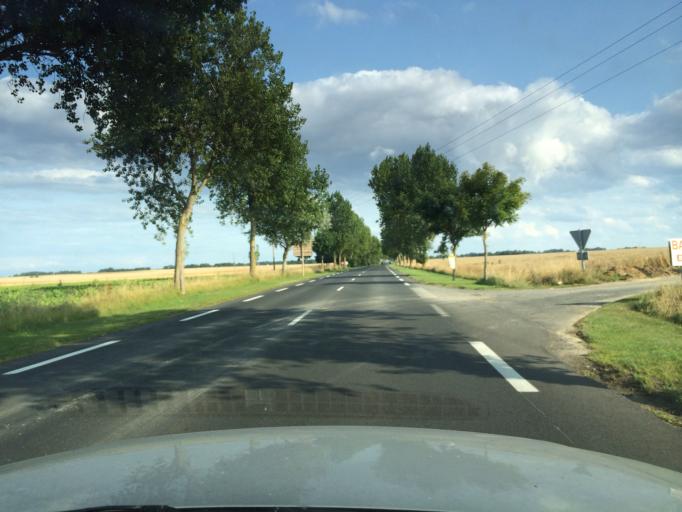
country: FR
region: Lower Normandy
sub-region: Departement du Calvados
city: Courseulles-sur-Mer
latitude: 49.3175
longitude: -0.4510
